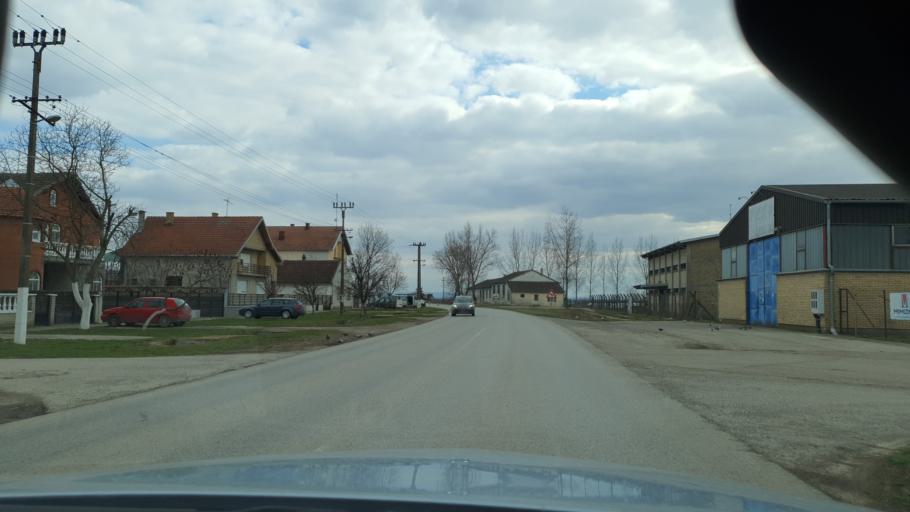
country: RS
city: Obrovac
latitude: 45.4116
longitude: 19.4052
